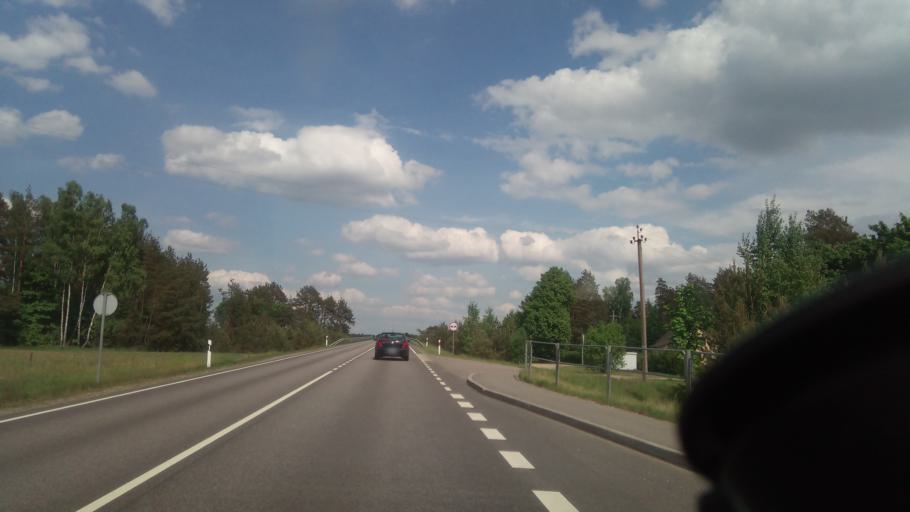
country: LT
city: Trakai
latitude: 54.6110
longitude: 24.8798
